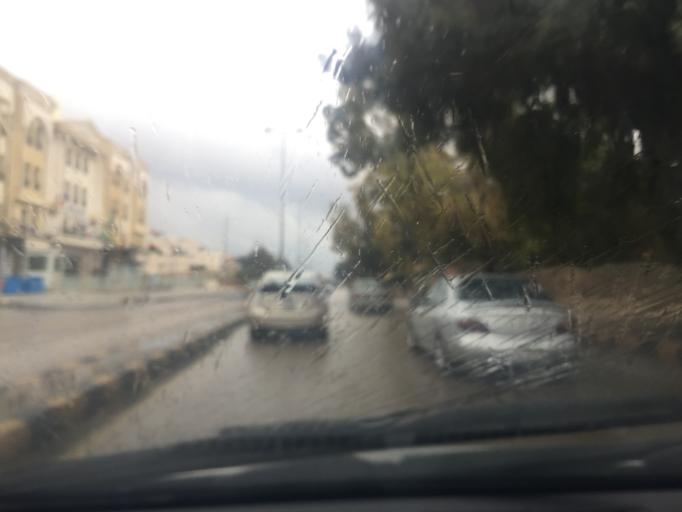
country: JO
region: Amman
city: Amman
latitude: 31.9977
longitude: 35.9314
